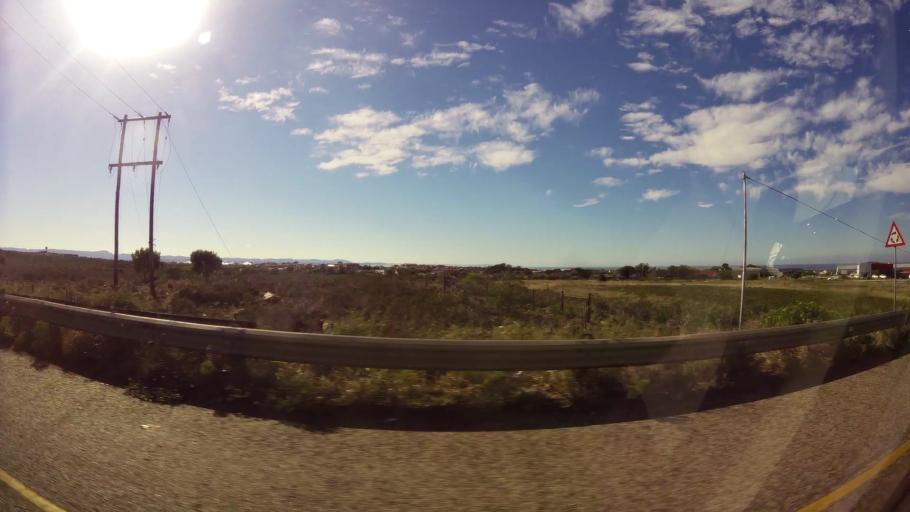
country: ZA
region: Eastern Cape
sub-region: Cacadu District Municipality
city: Jeffrey's Bay
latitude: -34.0279
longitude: 24.8998
